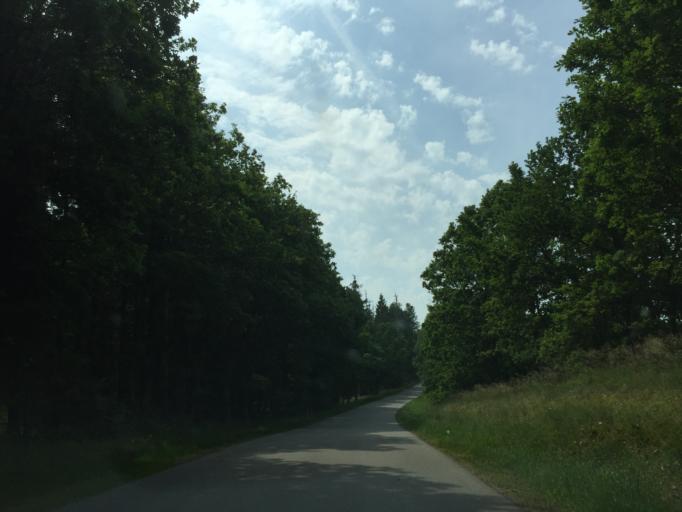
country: DK
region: Central Jutland
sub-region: Silkeborg Kommune
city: Virklund
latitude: 56.0521
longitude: 9.4566
